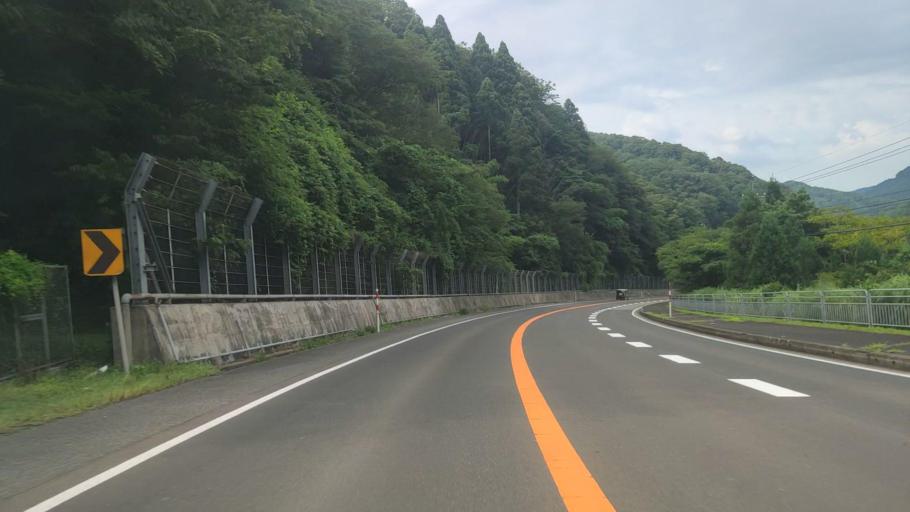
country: JP
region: Fukui
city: Takefu
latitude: 35.8092
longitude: 136.0951
